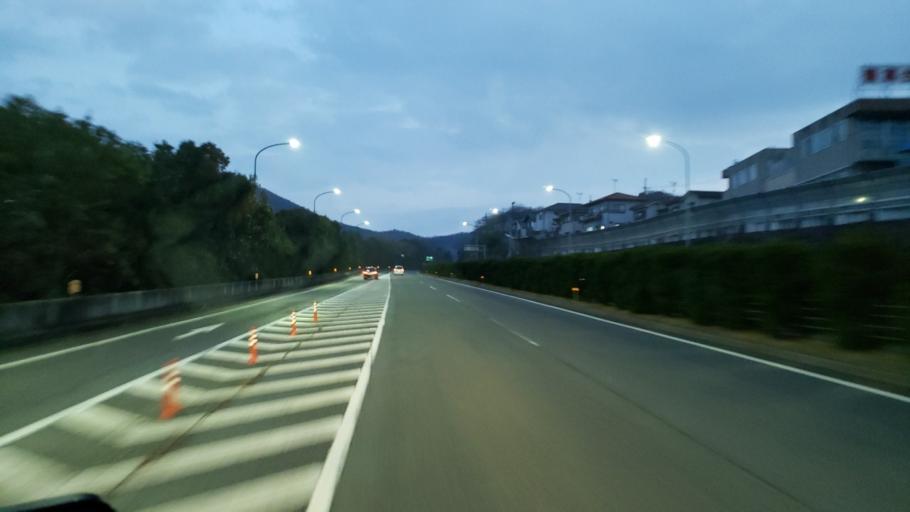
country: JP
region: Hyogo
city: Himeji
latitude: 34.8719
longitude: 134.7392
